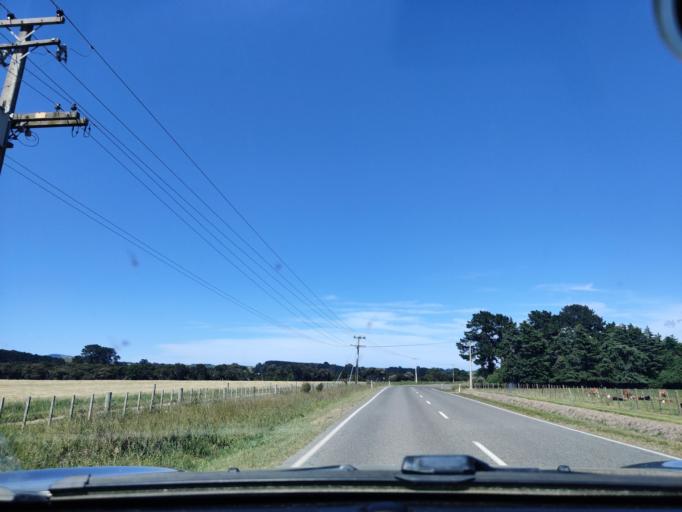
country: NZ
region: Wellington
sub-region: South Wairarapa District
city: Waipawa
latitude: -41.3112
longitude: 175.2669
